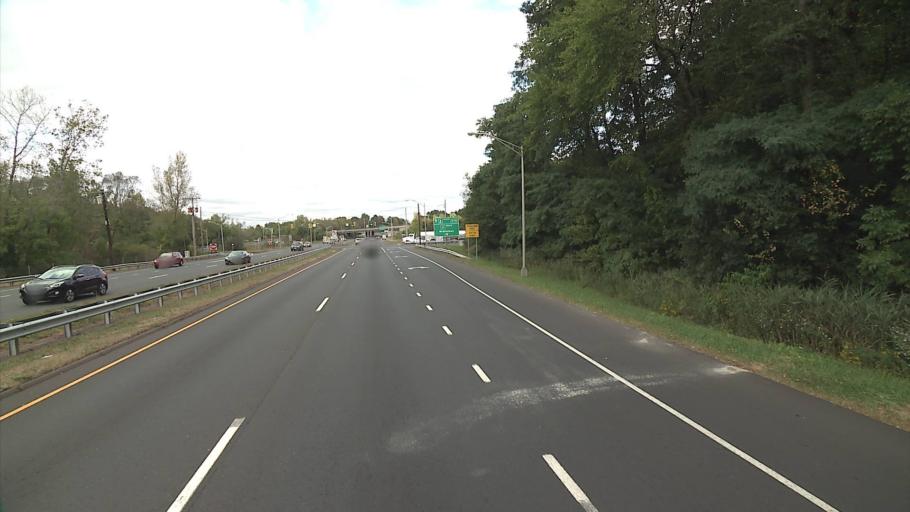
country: US
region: Connecticut
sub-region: Hartford County
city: Kensington
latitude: 41.6214
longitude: -72.7417
